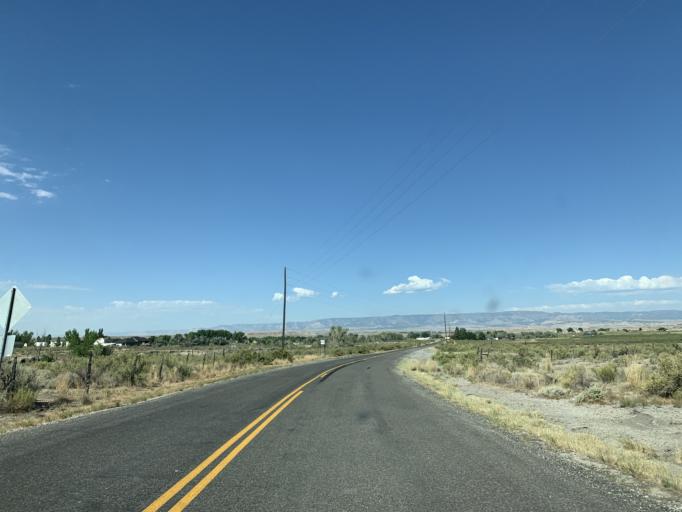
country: US
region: Utah
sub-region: Carbon County
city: Wellington
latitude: 39.5509
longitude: -110.6714
